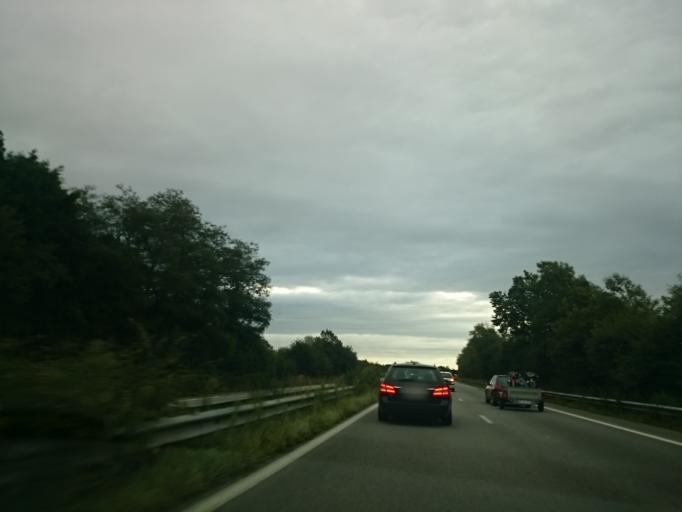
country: FR
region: Brittany
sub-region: Departement du Finistere
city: Saint-Yvi
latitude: 47.9658
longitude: -3.9750
